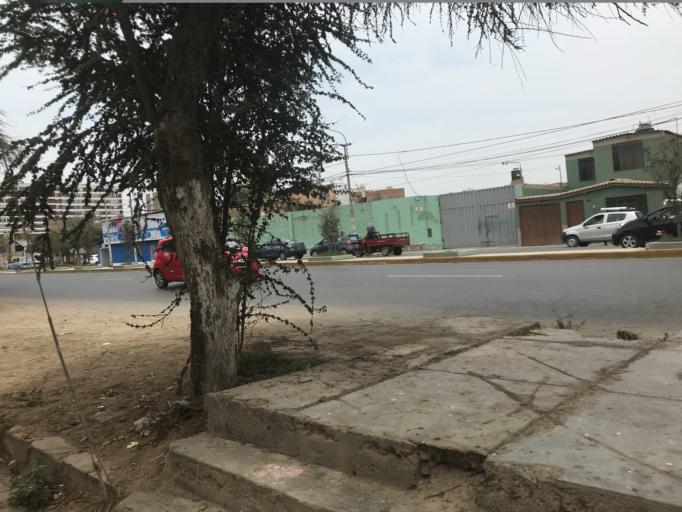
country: PE
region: Lambayeque
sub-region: Provincia de Chiclayo
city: Chiclayo
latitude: -6.7703
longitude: -79.8561
